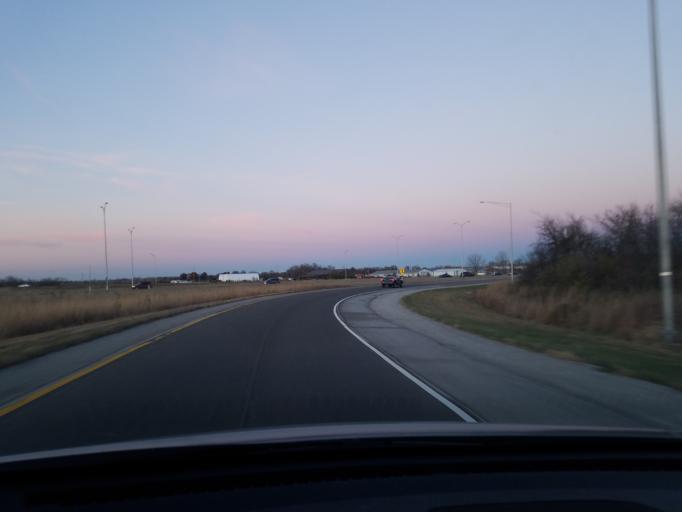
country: US
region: Illinois
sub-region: Saint Clair County
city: Washington Park
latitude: 38.6176
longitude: -90.0660
